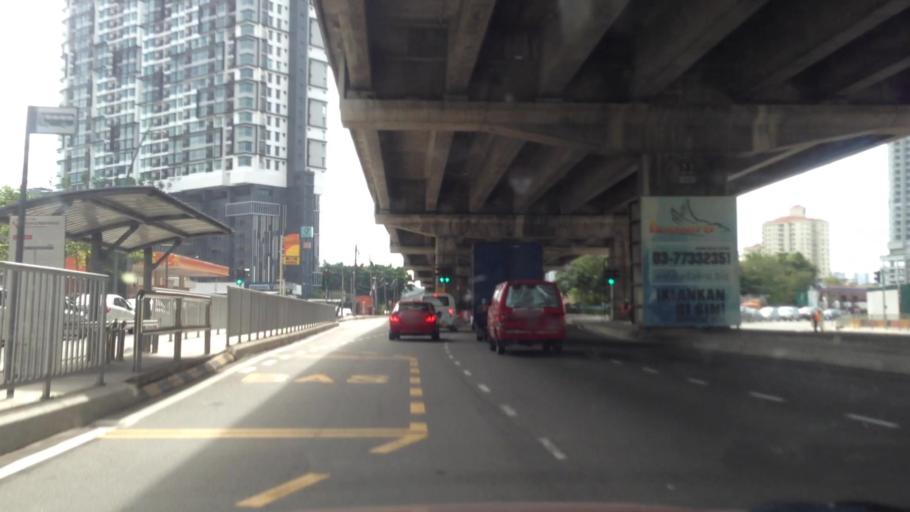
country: MY
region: Selangor
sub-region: Petaling
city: Petaling Jaya
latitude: 3.0834
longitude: 101.6612
